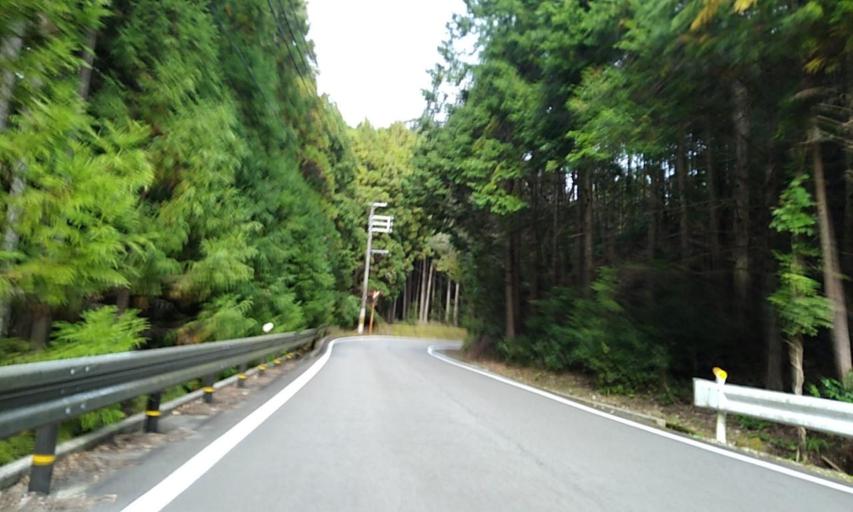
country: JP
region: Wakayama
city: Shingu
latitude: 33.5421
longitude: 135.8424
